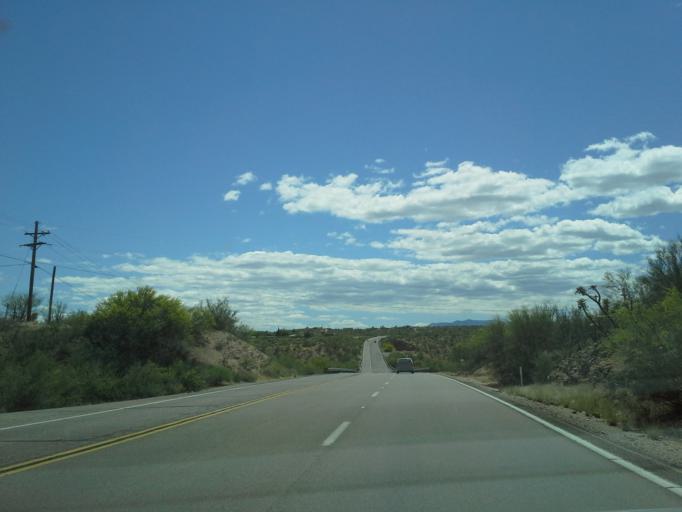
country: US
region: Arizona
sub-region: Pinal County
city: Mammoth
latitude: 32.7033
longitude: -110.6436
